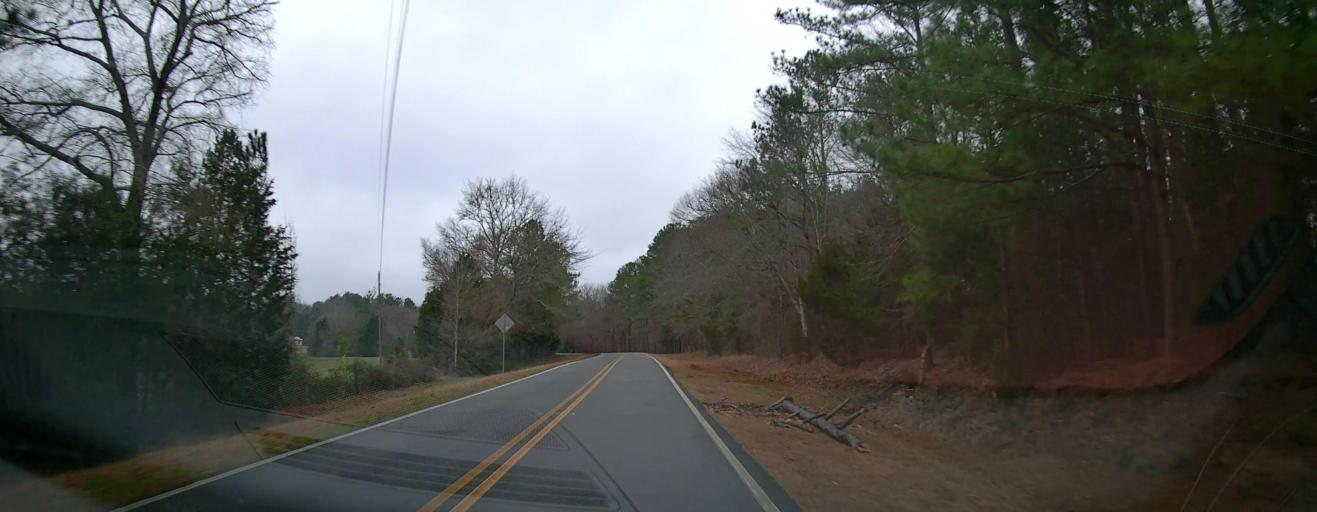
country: US
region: Georgia
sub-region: Monroe County
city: Forsyth
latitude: 33.1136
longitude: -83.9494
